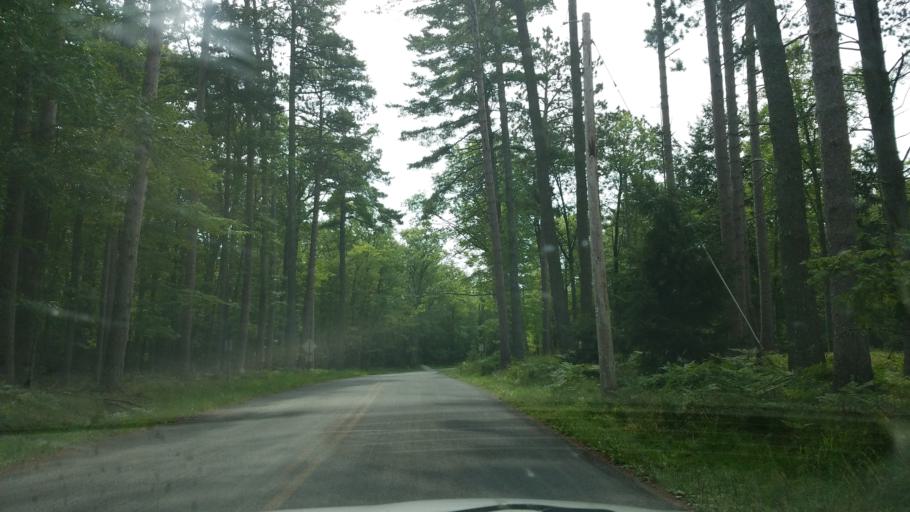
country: US
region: Wisconsin
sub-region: Bayfield County
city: Washburn
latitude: 46.7618
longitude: -90.7828
